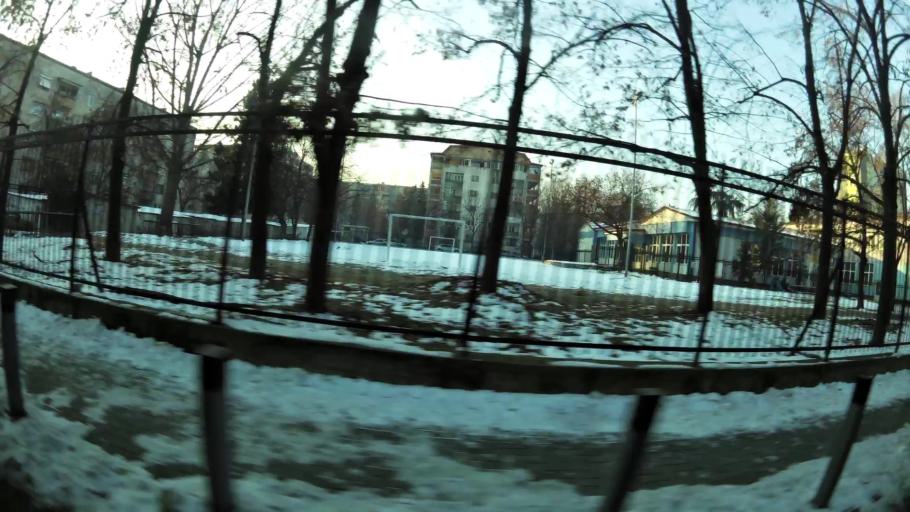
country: MK
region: Karpos
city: Skopje
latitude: 42.0038
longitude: 21.4096
